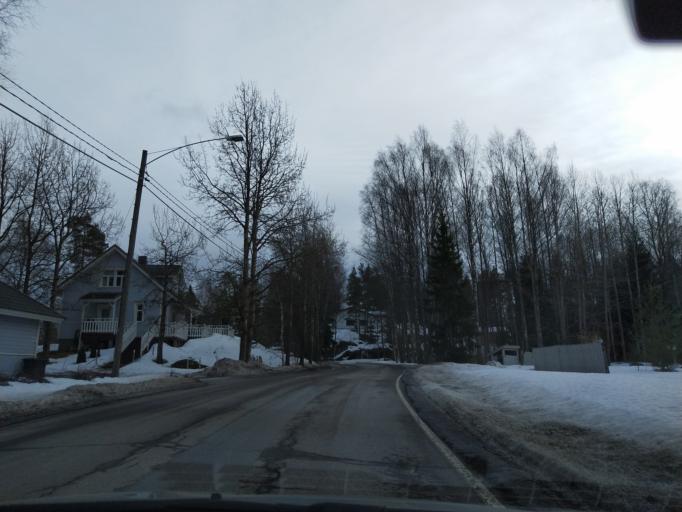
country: FI
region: Uusimaa
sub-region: Helsinki
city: Sibbo
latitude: 60.2648
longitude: 25.2872
